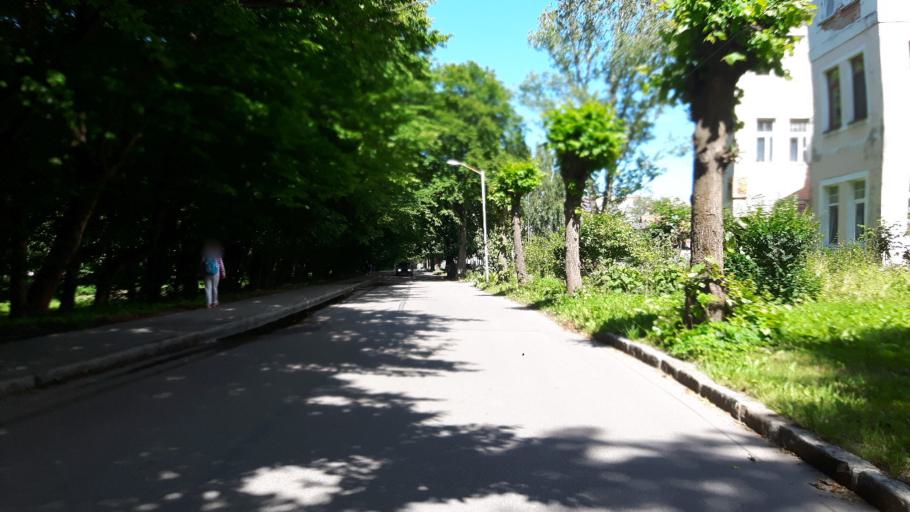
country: RU
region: Kaliningrad
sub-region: Zelenogradskiy Rayon
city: Zelenogradsk
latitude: 54.9616
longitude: 20.4890
